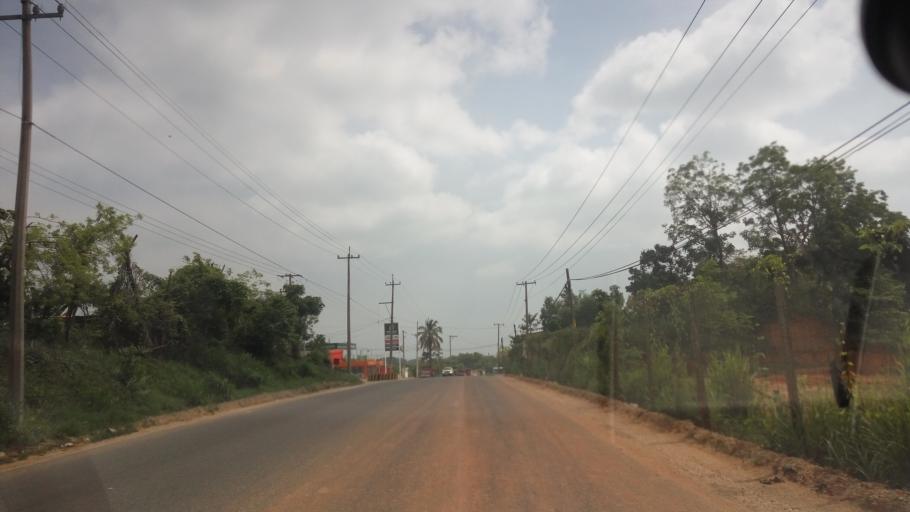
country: MX
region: Chiapas
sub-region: Reforma
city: El Carmen (El Limon)
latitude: 17.8810
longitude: -93.1491
